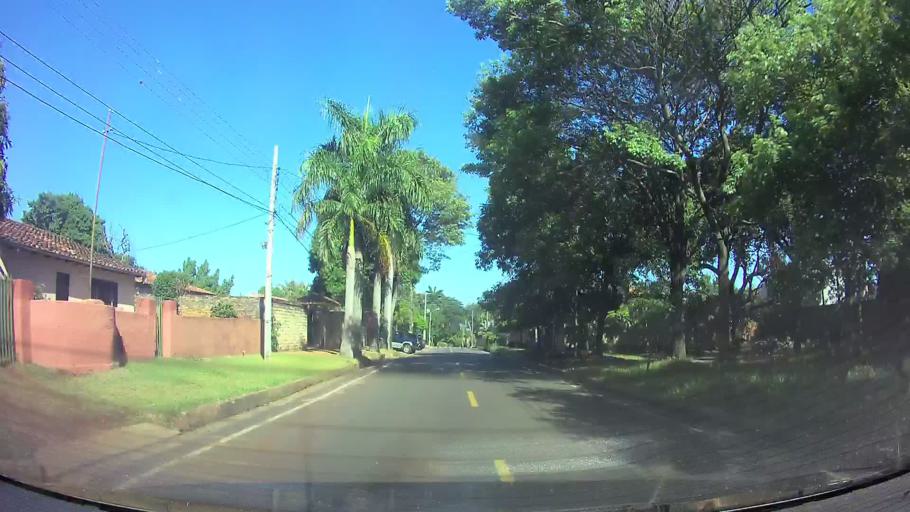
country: PY
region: Central
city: Fernando de la Mora
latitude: -25.2689
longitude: -57.5120
